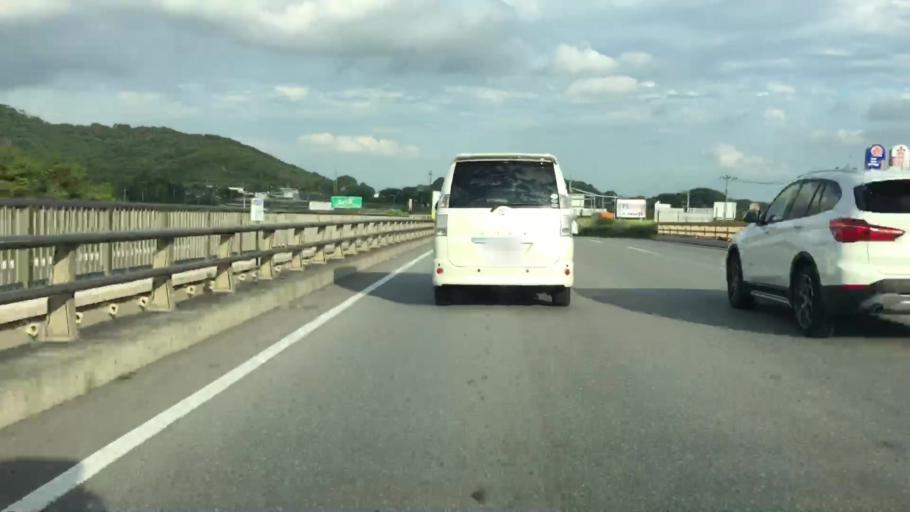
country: JP
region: Tochigi
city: Sano
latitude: 36.2962
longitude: 139.6068
